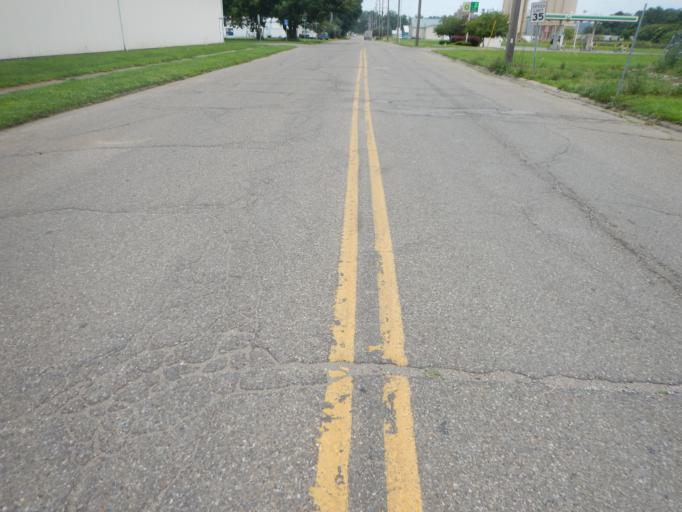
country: US
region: Ohio
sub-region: Muskingum County
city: Zanesville
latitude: 39.9457
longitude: -82.0195
